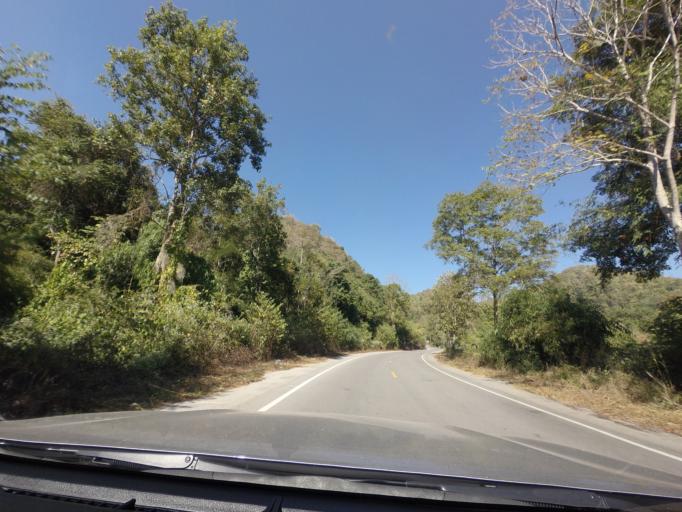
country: TH
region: Lampang
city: Chae Hom
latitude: 18.5547
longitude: 99.6254
